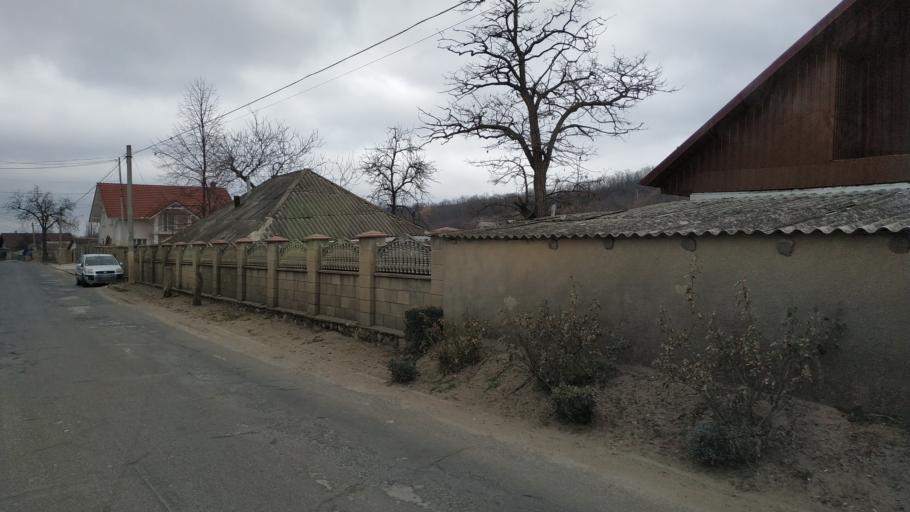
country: MD
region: Laloveni
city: Ialoveni
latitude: 46.9032
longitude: 28.8068
